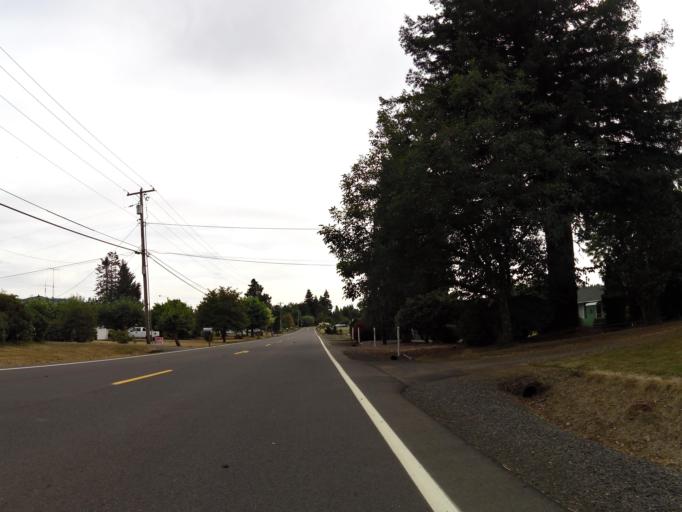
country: US
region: Washington
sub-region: Cowlitz County
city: West Side Highway
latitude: 46.2226
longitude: -122.8950
